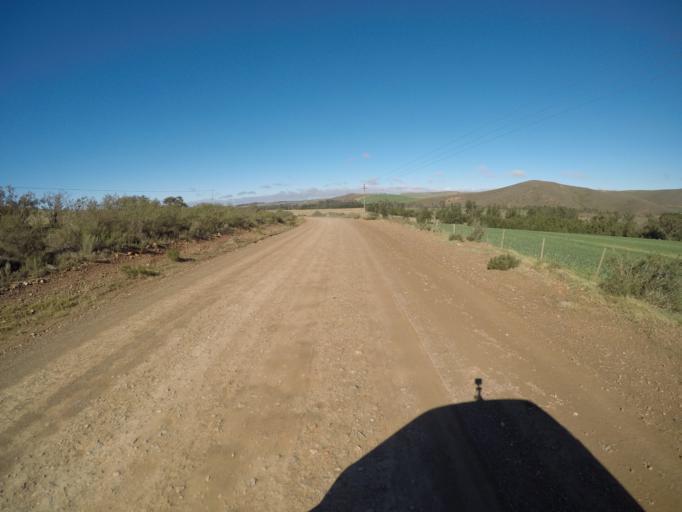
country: ZA
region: Western Cape
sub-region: Overberg District Municipality
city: Caledon
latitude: -34.0822
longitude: 19.6468
